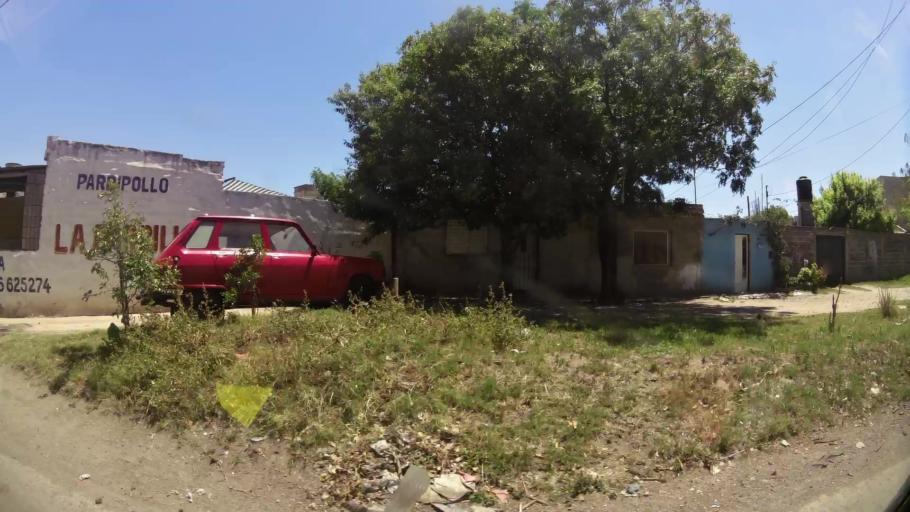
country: AR
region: Cordoba
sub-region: Departamento de Capital
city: Cordoba
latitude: -31.3847
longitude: -64.1479
